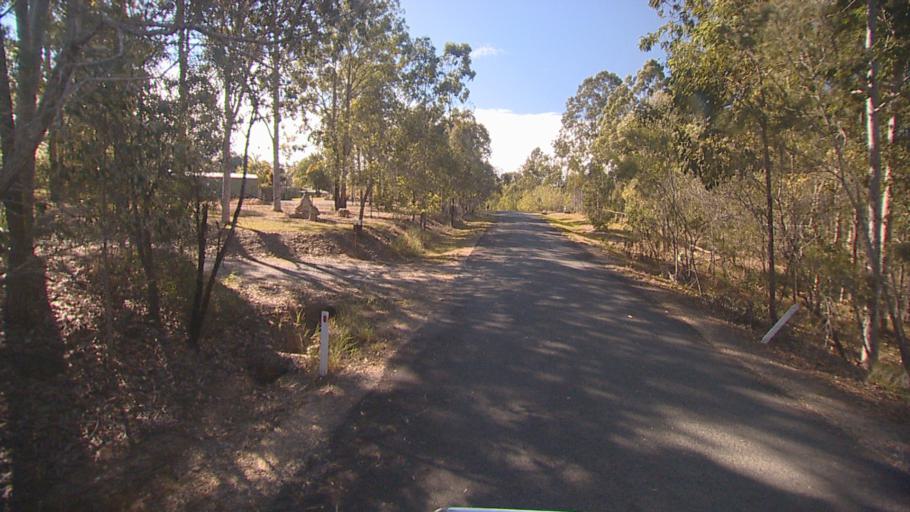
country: AU
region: Queensland
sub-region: Ipswich
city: Springfield Lakes
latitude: -27.7128
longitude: 152.9256
